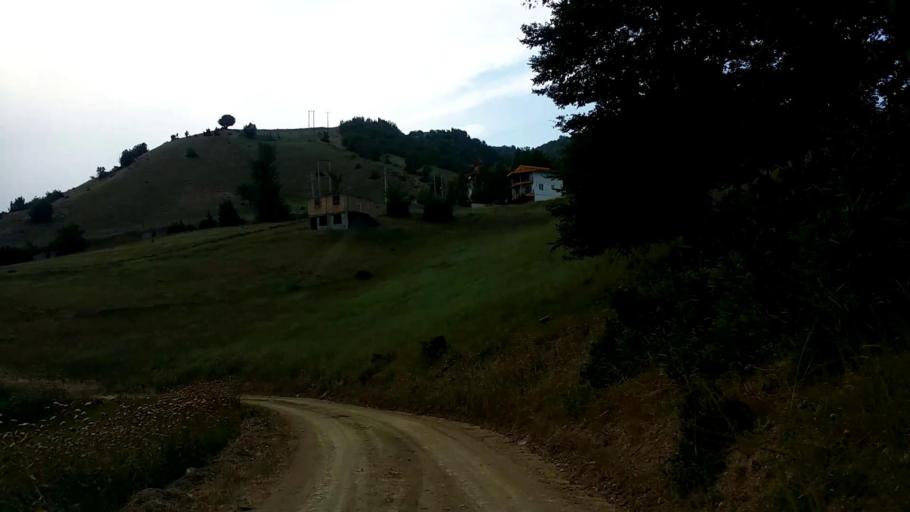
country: IR
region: Mazandaran
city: Chalus
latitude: 36.5528
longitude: 51.2910
